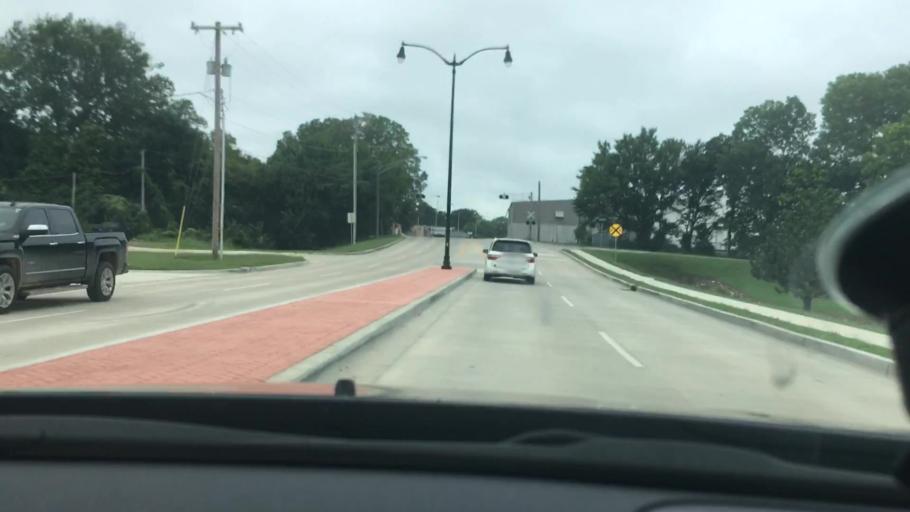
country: US
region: Oklahoma
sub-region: Pontotoc County
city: Ada
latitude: 34.7818
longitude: -96.6728
